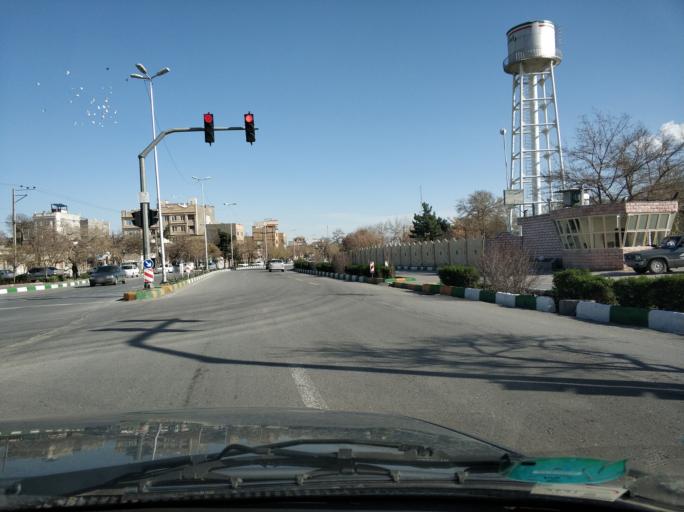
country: IR
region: Razavi Khorasan
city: Mashhad
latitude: 36.3017
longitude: 59.6311
